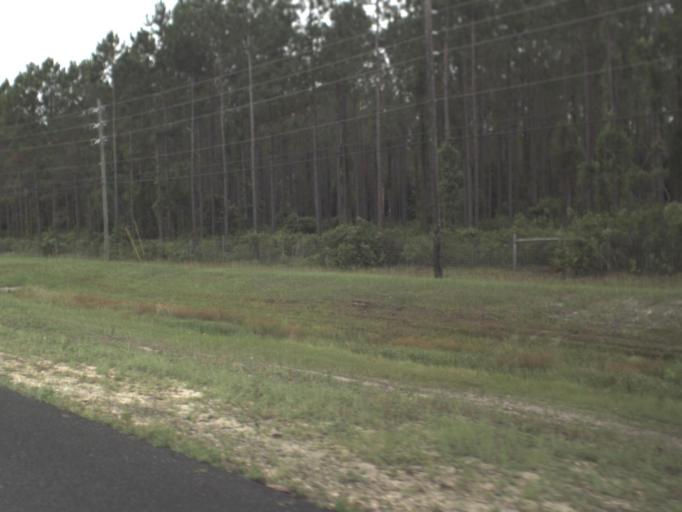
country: US
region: Florida
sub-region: Nassau County
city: Yulee
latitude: 30.6128
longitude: -81.6778
